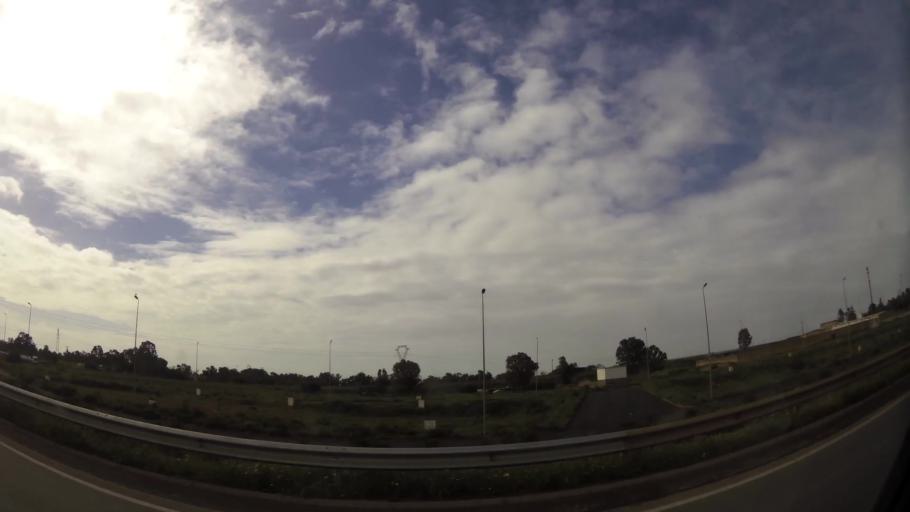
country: MA
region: Grand Casablanca
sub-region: Mohammedia
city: Mohammedia
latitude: 33.6457
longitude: -7.4189
